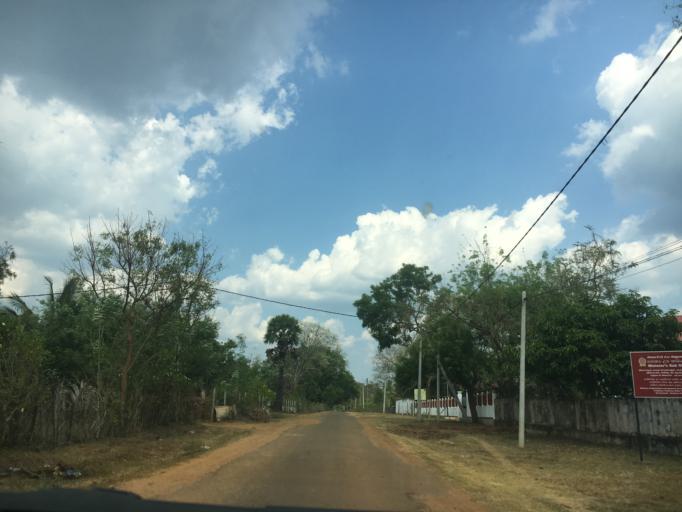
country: LK
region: Northern Province
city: Kilinochchi
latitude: 9.1410
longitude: 80.4422
